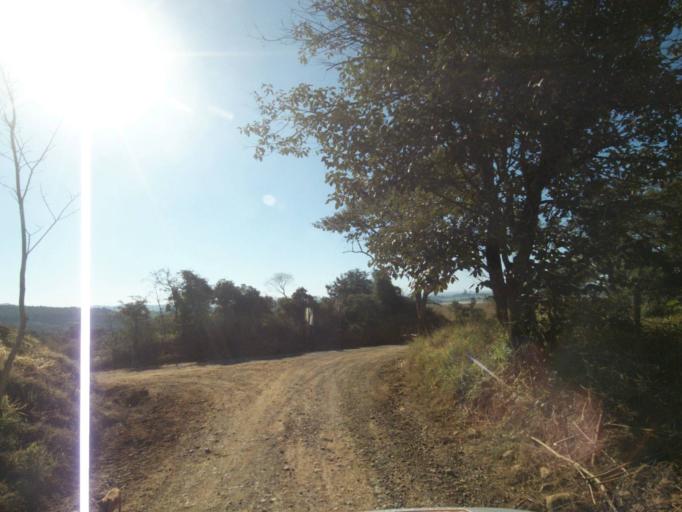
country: BR
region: Parana
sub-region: Tibagi
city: Tibagi
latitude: -24.5391
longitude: -50.4683
